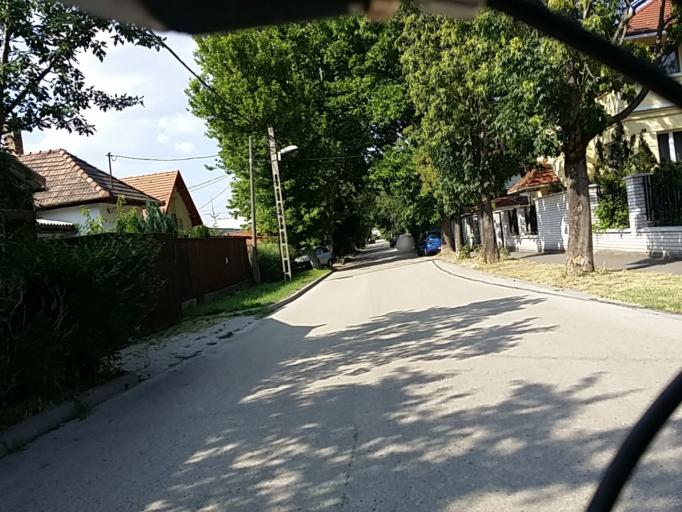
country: HU
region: Budapest
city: Budapest IV. keruelet
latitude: 47.5772
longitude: 19.0603
